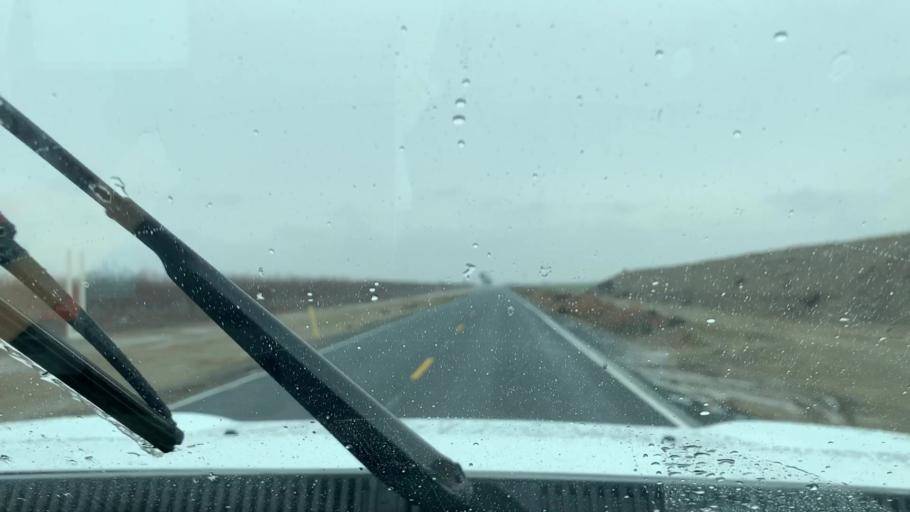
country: US
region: California
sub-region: Tulare County
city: Earlimart
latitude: 35.8918
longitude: -119.3689
